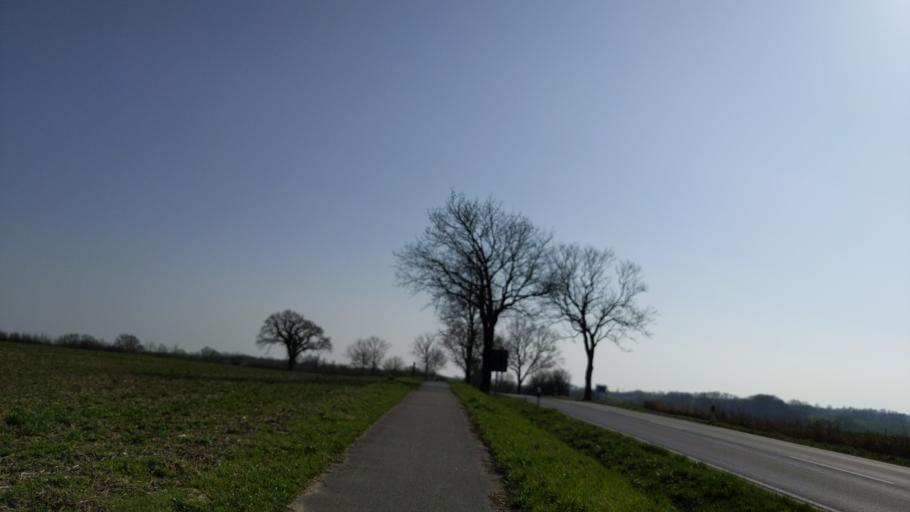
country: DE
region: Schleswig-Holstein
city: Altenkrempe
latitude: 54.1307
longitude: 10.8479
